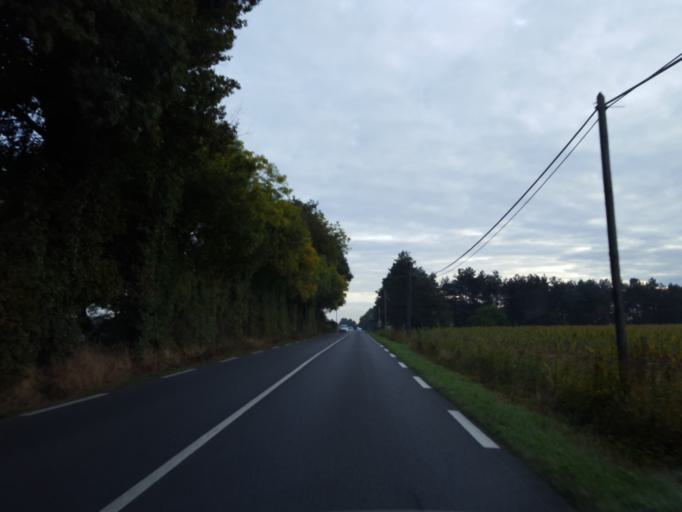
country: FR
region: Pays de la Loire
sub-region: Departement de la Loire-Atlantique
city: Haute-Goulaine
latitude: 47.2261
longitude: -1.4180
